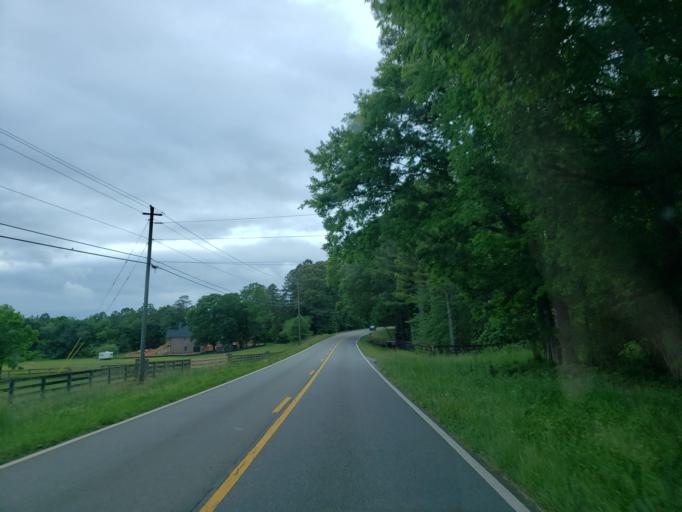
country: US
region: Georgia
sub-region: Bartow County
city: Euharlee
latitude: 34.1740
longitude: -84.9833
